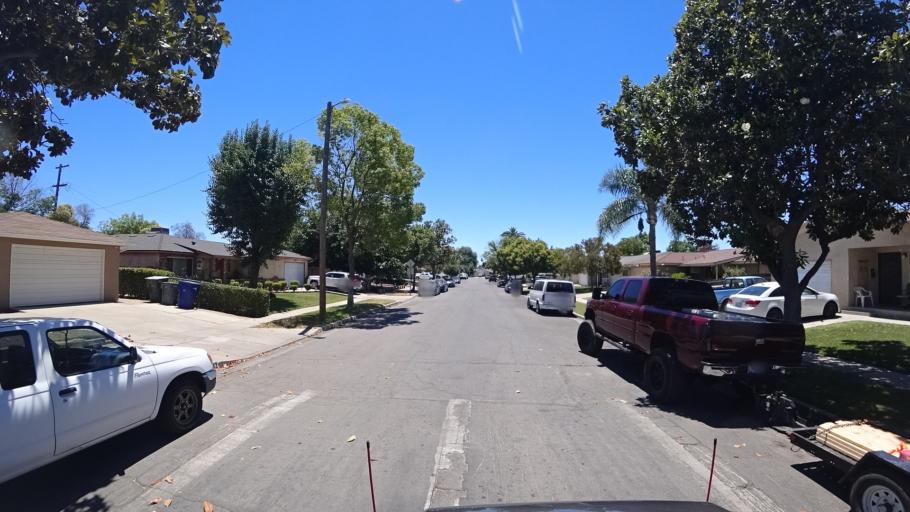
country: US
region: California
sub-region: Fresno County
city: West Park
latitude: 36.7889
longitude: -119.8403
